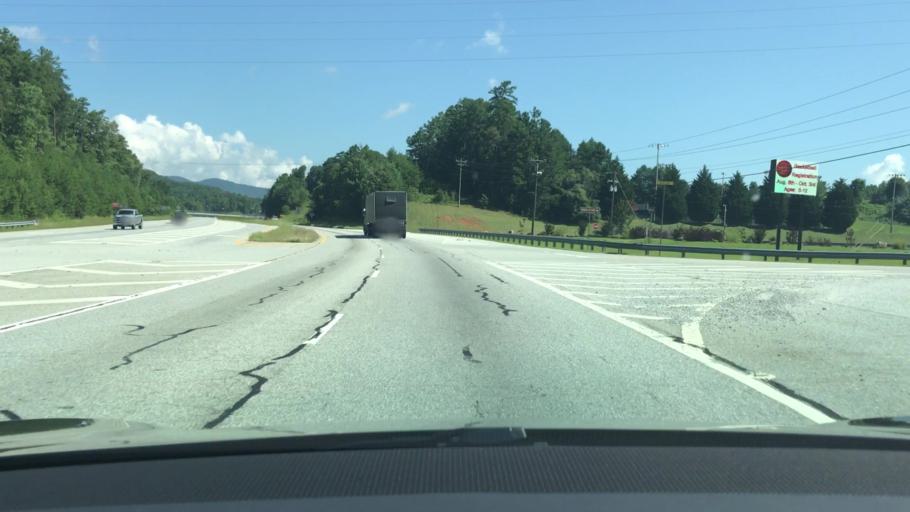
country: US
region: Georgia
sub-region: Rabun County
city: Clayton
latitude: 34.8201
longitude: -83.4234
